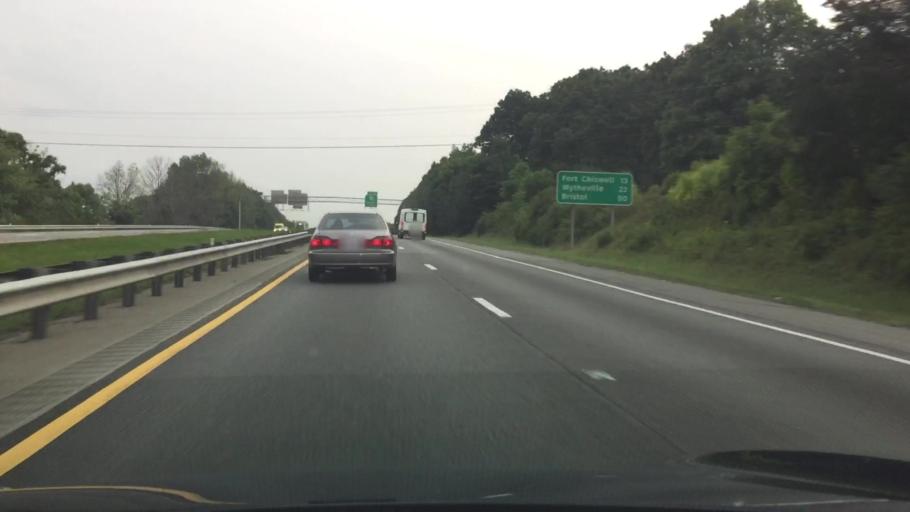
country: US
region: Virginia
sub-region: Pulaski County
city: Pulaski
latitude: 37.0193
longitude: -80.7363
